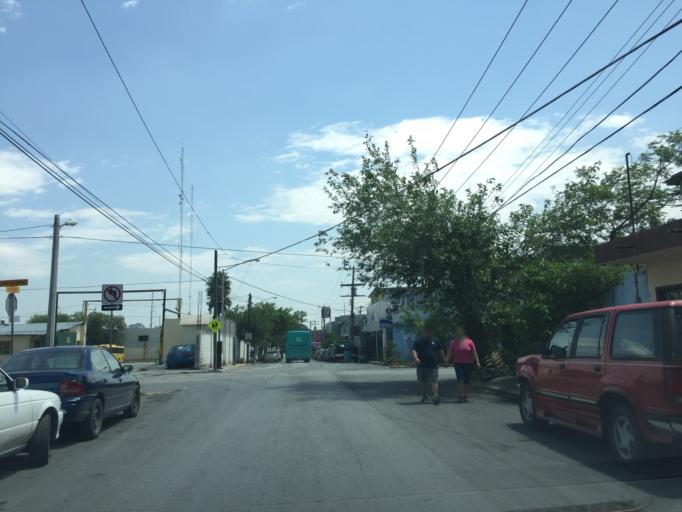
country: MX
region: Nuevo Leon
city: Apodaca
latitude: 25.7812
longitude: -100.1826
